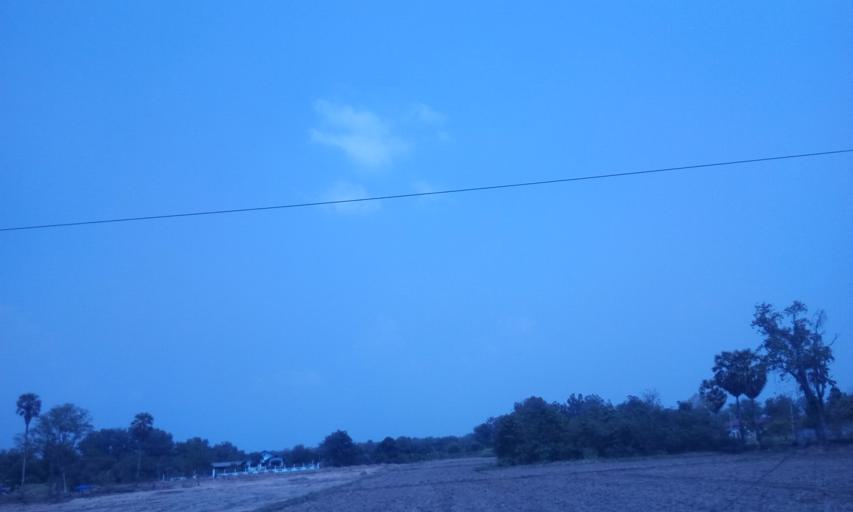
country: TH
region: Chon Buri
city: Phanat Nikhom
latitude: 13.4271
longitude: 101.1840
